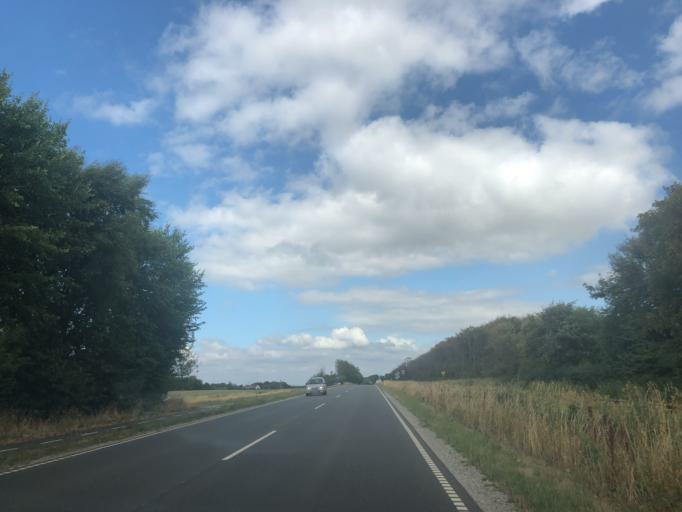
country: DK
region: Central Jutland
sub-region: Struer Kommune
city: Struer
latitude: 56.4660
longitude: 8.6848
